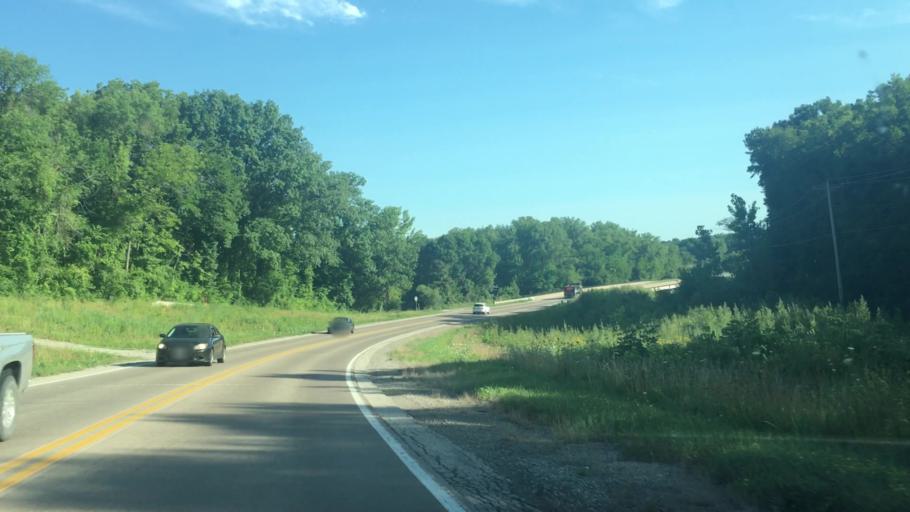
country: US
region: Iowa
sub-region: Johnson County
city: Iowa City
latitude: 41.6916
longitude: -91.5470
